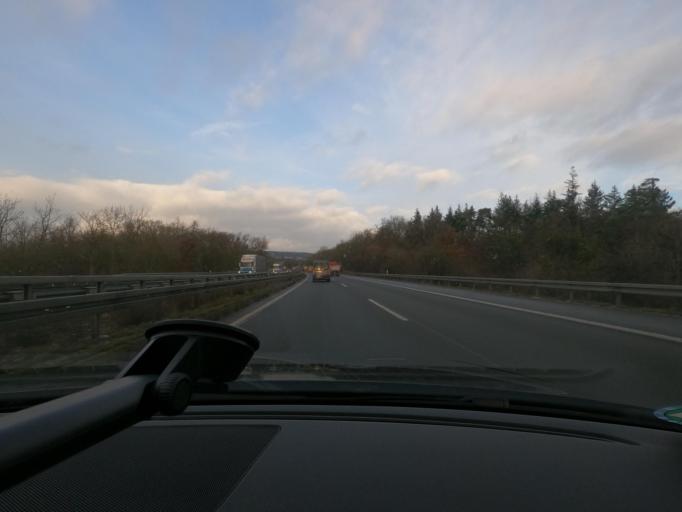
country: DE
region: Hesse
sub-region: Regierungsbezirk Kassel
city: Breuna
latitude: 51.3937
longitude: 9.2126
